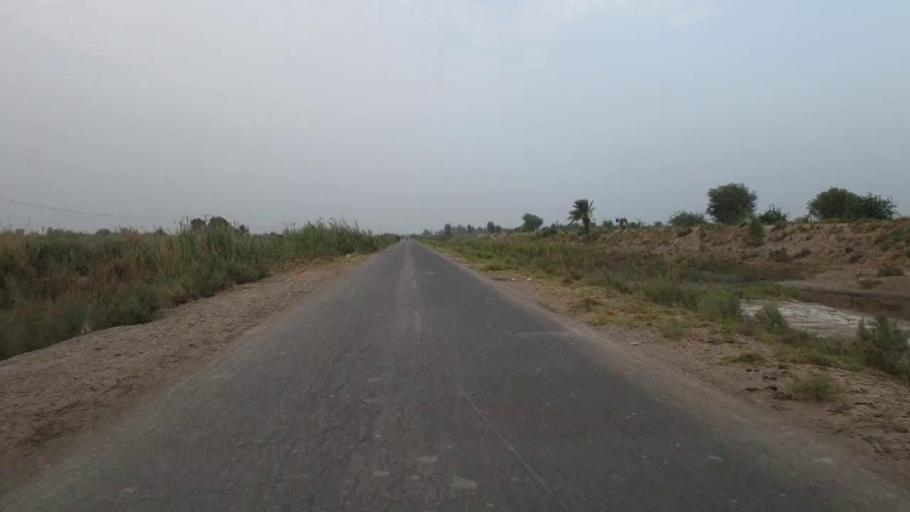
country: PK
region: Sindh
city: Daur
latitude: 26.4492
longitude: 68.2868
